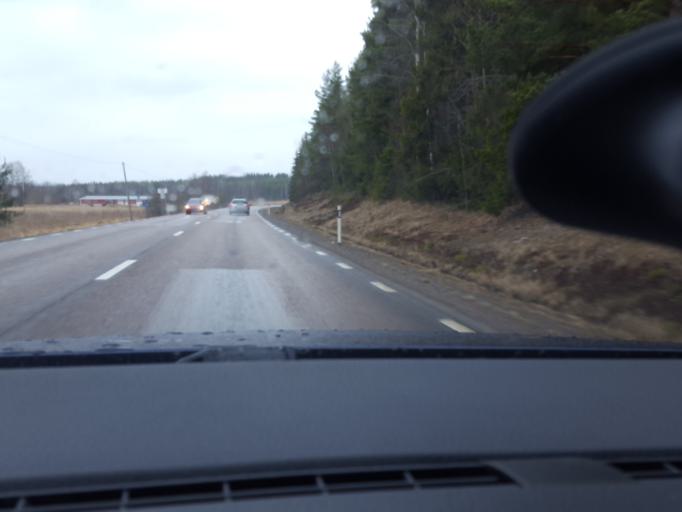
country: SE
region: Vaermland
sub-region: Sunne Kommun
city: Sunne
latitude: 59.6318
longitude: 12.9492
